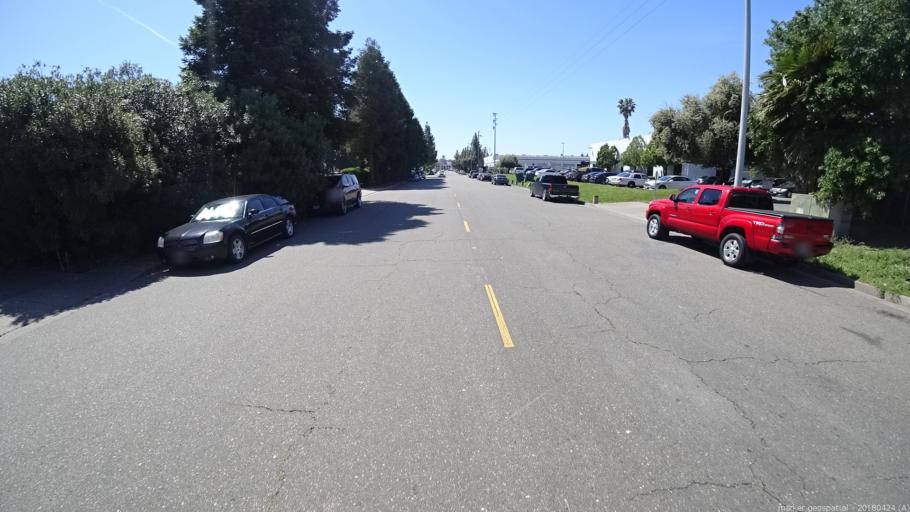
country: US
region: California
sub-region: Yolo County
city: West Sacramento
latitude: 38.5738
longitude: -121.5462
